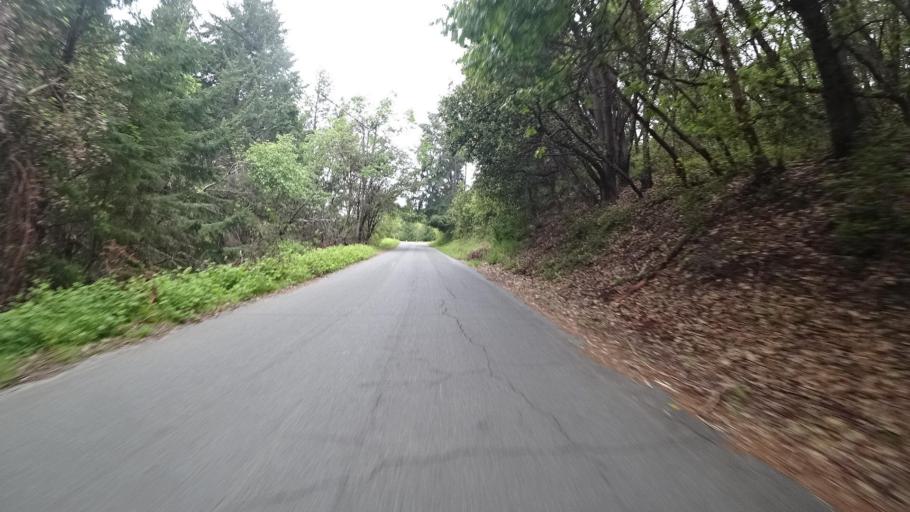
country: US
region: California
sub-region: Humboldt County
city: Willow Creek
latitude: 41.1123
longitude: -123.7157
